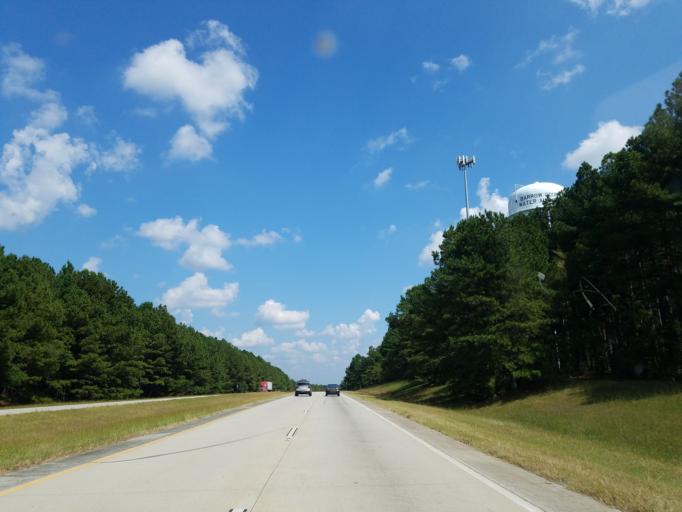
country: US
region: Georgia
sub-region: Barrow County
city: Russell
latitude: 33.9577
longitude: -83.6514
